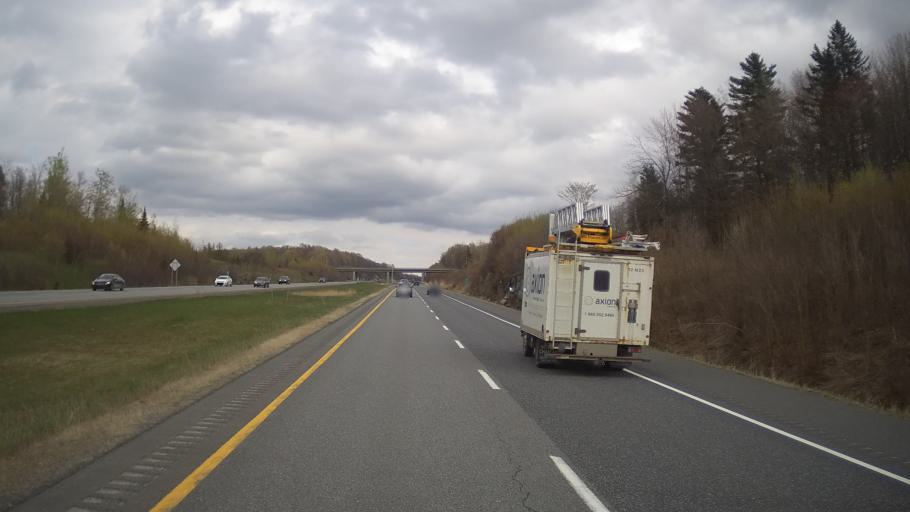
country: CA
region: Quebec
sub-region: Monteregie
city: Waterloo
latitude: 45.3025
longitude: -72.4260
